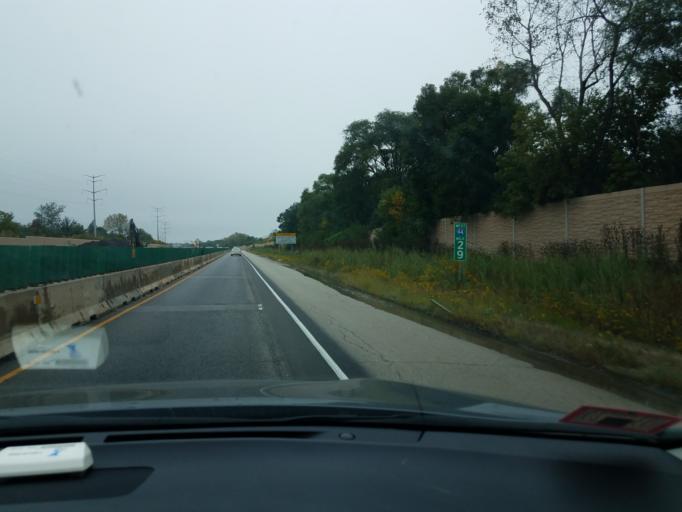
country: US
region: Illinois
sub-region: Cook County
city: Northbrook
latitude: 42.1459
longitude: -87.8062
